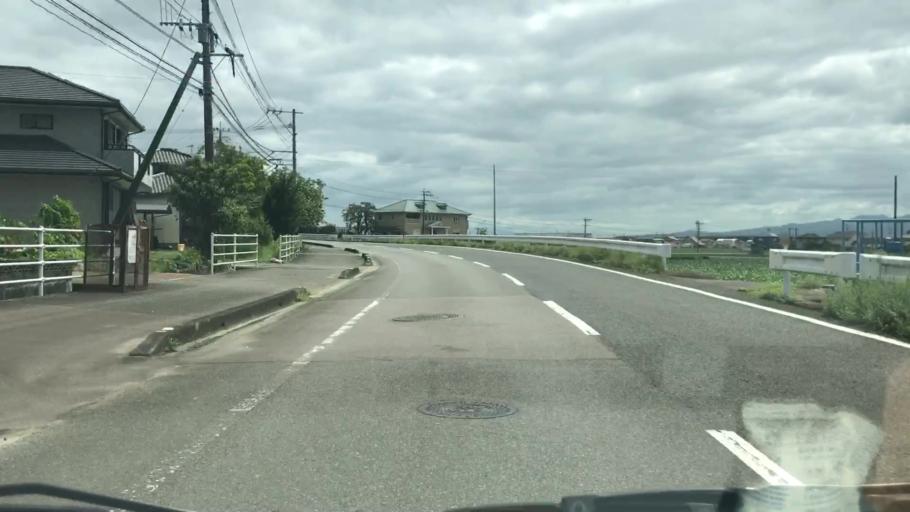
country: JP
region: Saga Prefecture
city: Kashima
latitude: 33.2281
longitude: 130.1534
